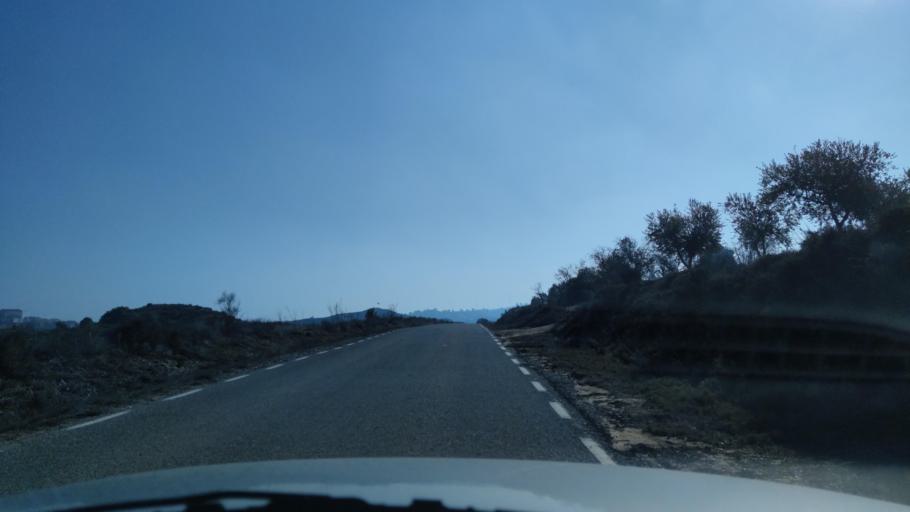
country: ES
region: Catalonia
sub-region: Provincia de Lleida
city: Torrebesses
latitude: 41.4296
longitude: 0.5839
